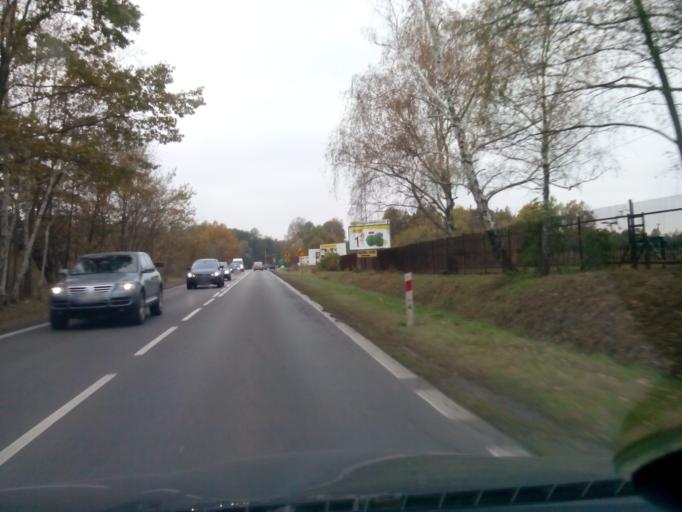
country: PL
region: Masovian Voivodeship
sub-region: Powiat grodziski
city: Podkowa Lesna
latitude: 52.1310
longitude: 20.7228
